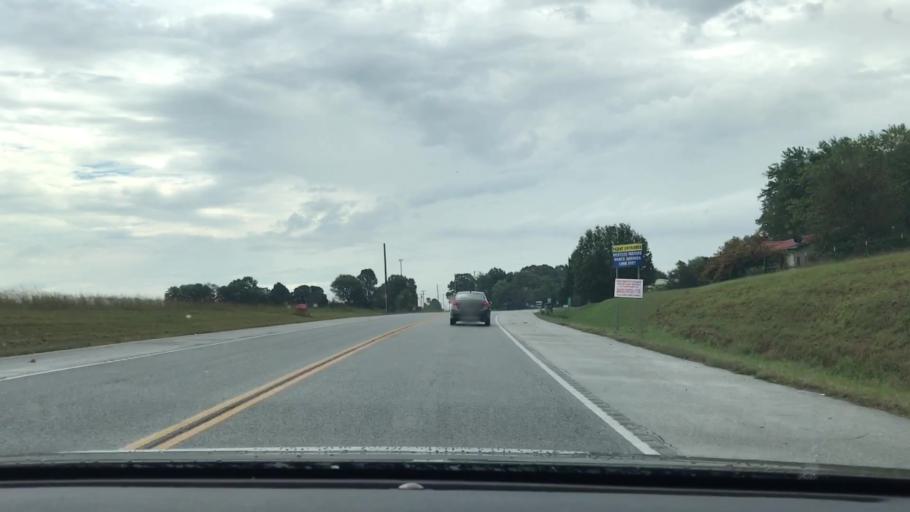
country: US
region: Tennessee
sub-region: Macon County
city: Red Boiling Springs
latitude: 36.5229
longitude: -85.8721
